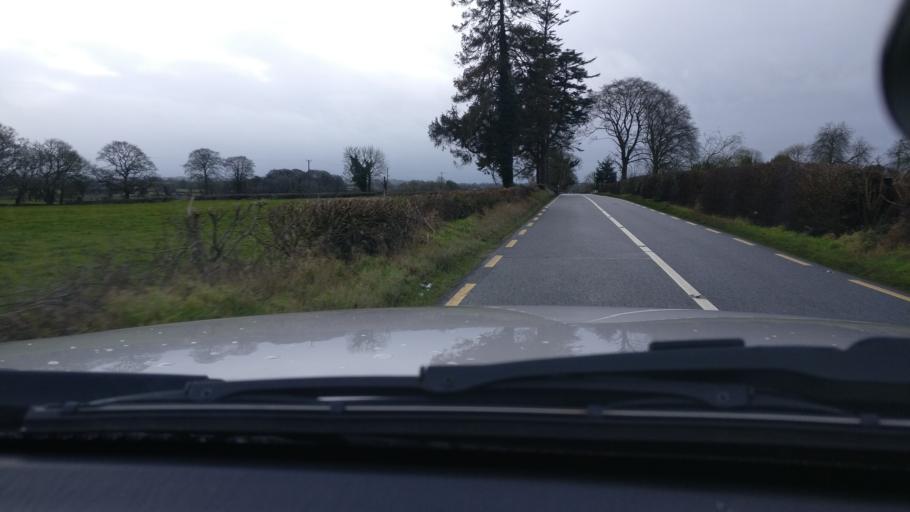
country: IE
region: Leinster
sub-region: An Longfort
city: Ballymahon
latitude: 53.5448
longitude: -7.7834
